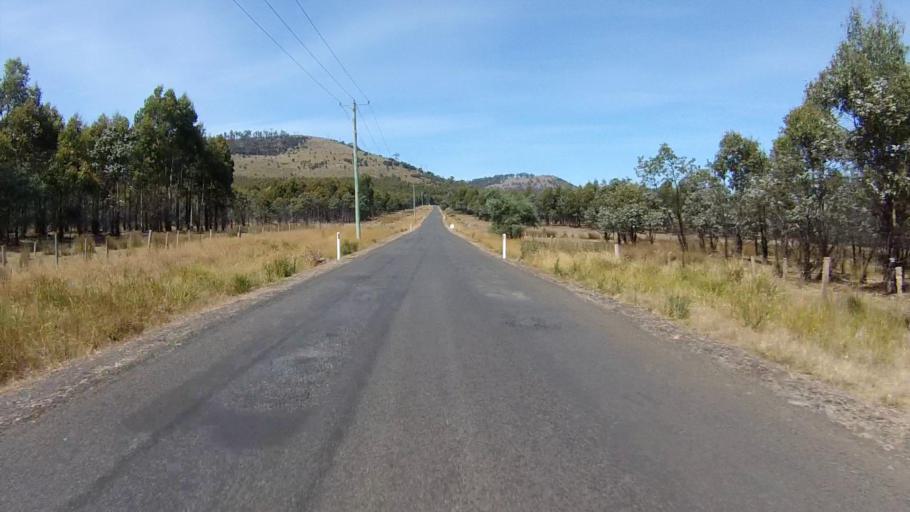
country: AU
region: Tasmania
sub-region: Sorell
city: Sorell
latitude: -42.6195
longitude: 147.7301
